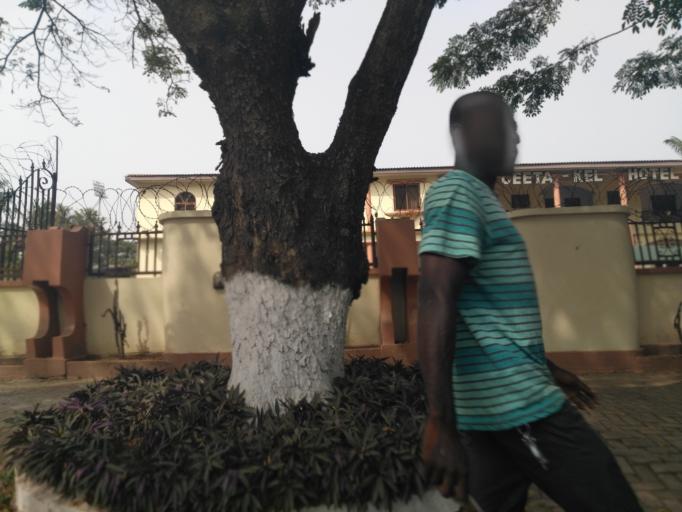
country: GH
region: Ashanti
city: Kumasi
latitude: 6.6798
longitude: -1.6032
